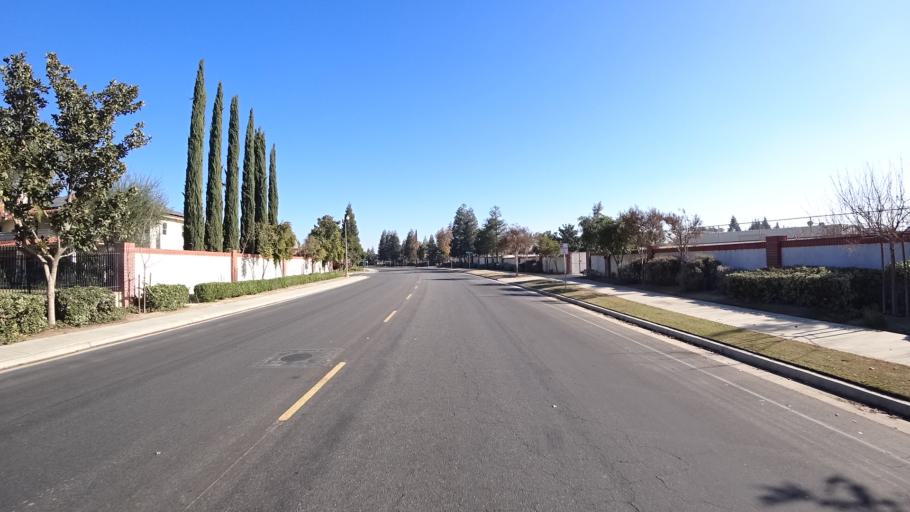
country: US
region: California
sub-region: Kern County
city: Greenacres
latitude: 35.3286
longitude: -119.1218
